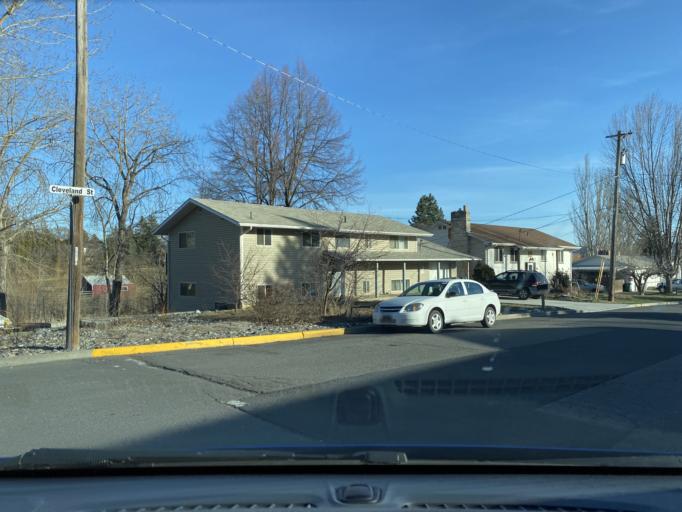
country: US
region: Idaho
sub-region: Latah County
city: Moscow
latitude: 46.7446
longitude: -116.9832
